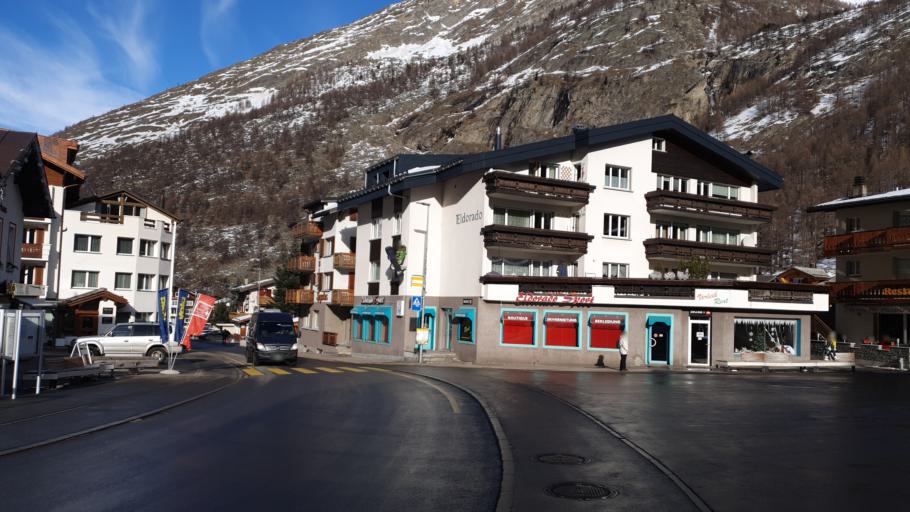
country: CH
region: Valais
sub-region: Visp District
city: Saas-Fee
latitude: 46.0942
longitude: 7.9575
